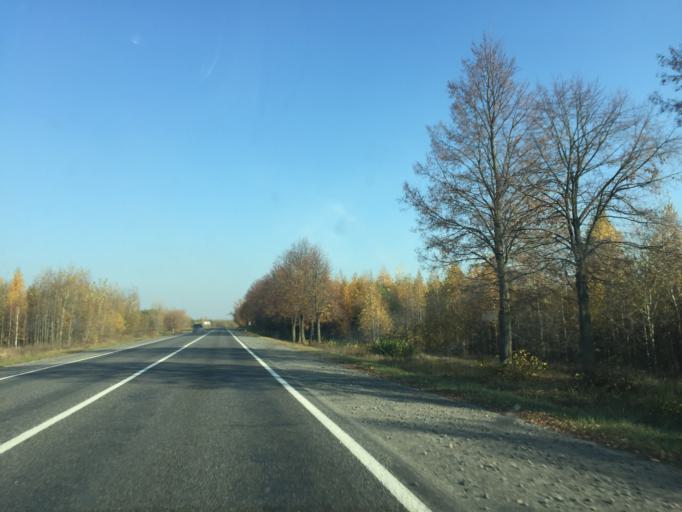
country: BY
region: Gomel
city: Dobrush
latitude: 52.3880
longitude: 31.4496
